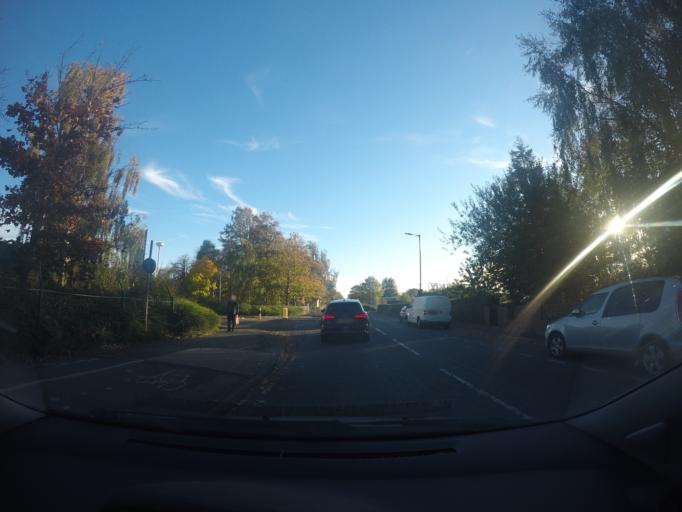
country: GB
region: England
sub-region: City of York
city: York
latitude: 53.9750
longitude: -1.0820
